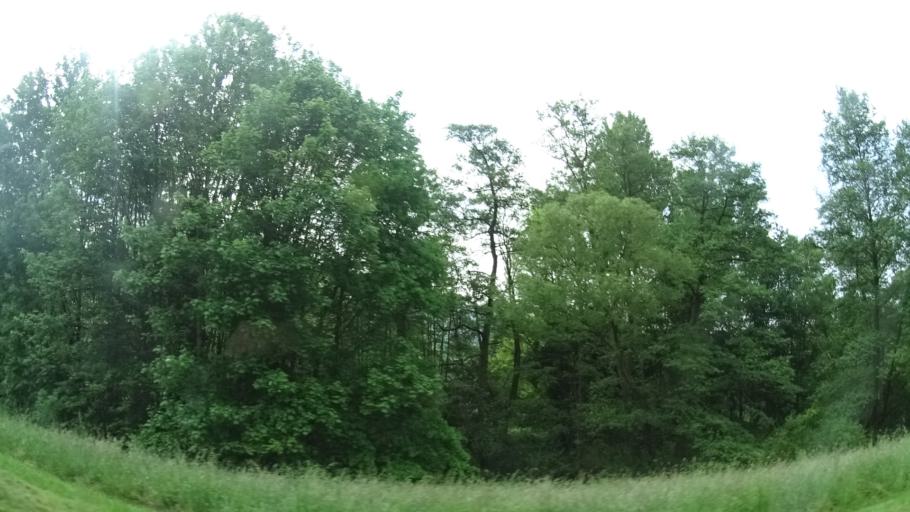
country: DE
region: Bavaria
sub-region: Regierungsbezirk Unterfranken
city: Eschau
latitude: 49.8326
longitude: 9.2635
